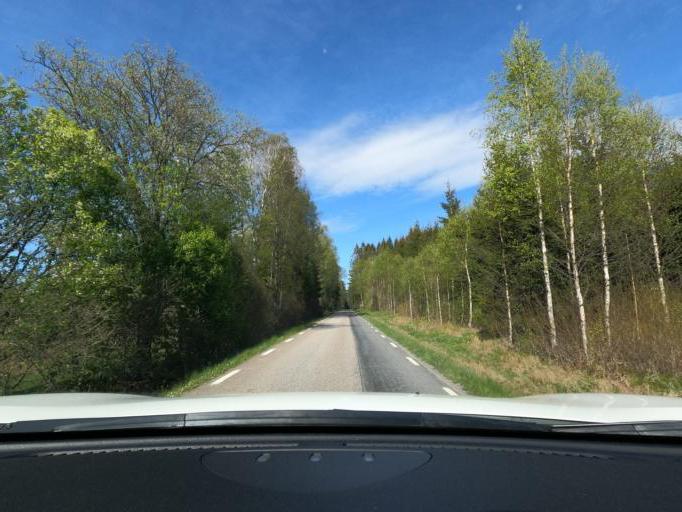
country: SE
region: Vaestra Goetaland
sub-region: Marks Kommun
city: Horred
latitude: 57.4427
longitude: 12.4318
